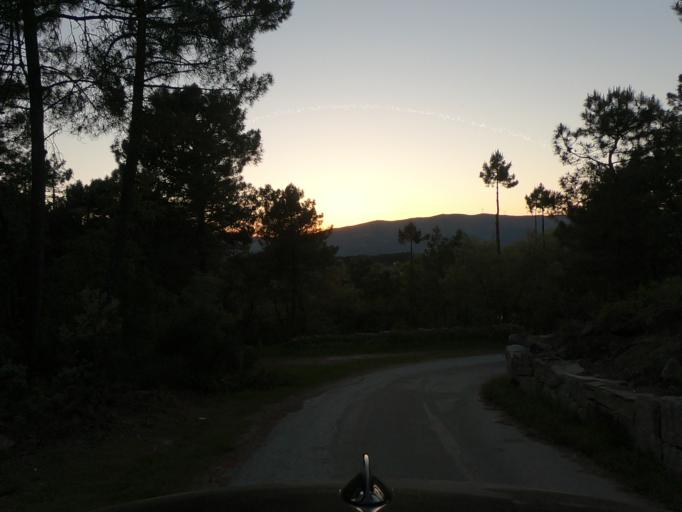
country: PT
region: Vila Real
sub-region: Vila Real
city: Vila Real
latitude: 41.3108
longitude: -7.6711
